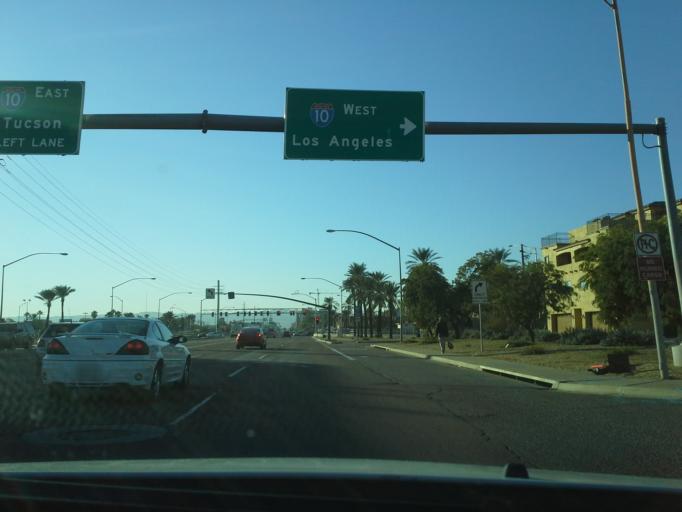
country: US
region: Arizona
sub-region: Maricopa County
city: Phoenix
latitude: 33.4640
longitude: -112.0653
